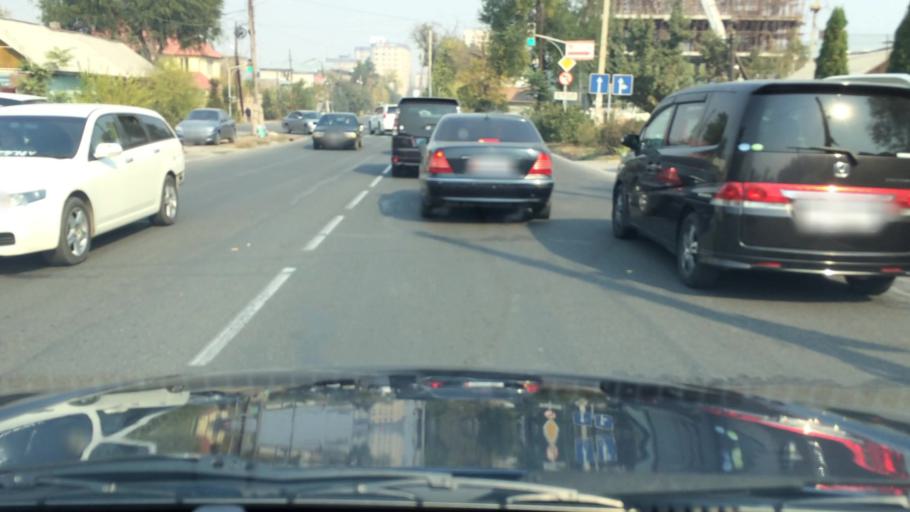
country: KG
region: Chuy
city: Bishkek
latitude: 42.8597
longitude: 74.5999
